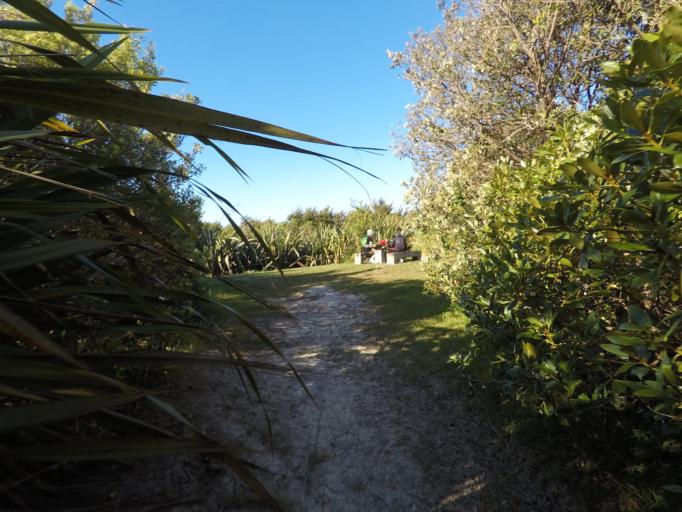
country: NZ
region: Auckland
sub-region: Auckland
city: Rosebank
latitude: -36.8381
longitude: 174.6615
